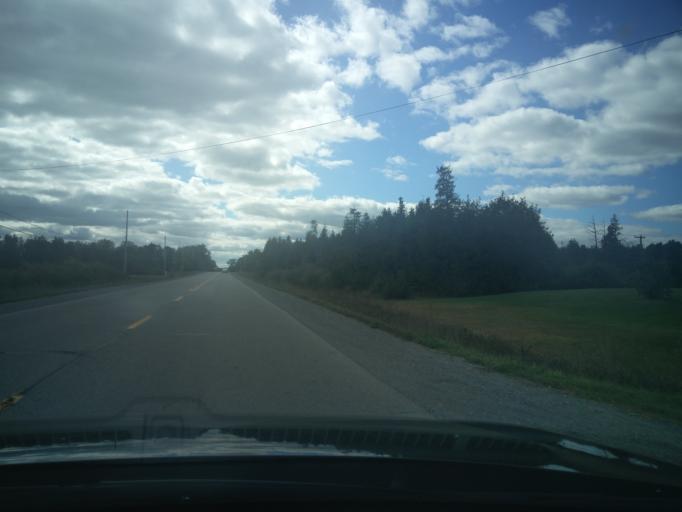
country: CA
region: Ontario
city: Carleton Place
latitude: 45.0608
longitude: -76.0420
